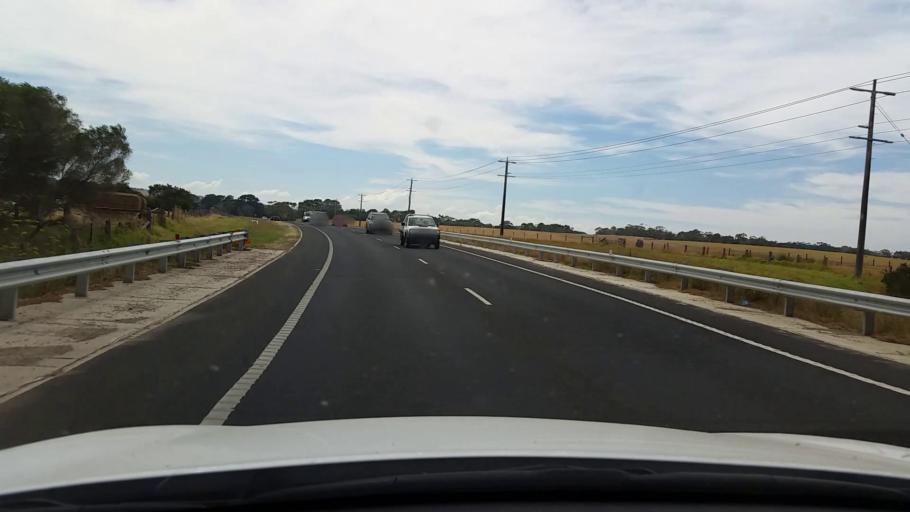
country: AU
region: Victoria
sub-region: Mornington Peninsula
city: Safety Beach
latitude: -38.3280
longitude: 145.0117
